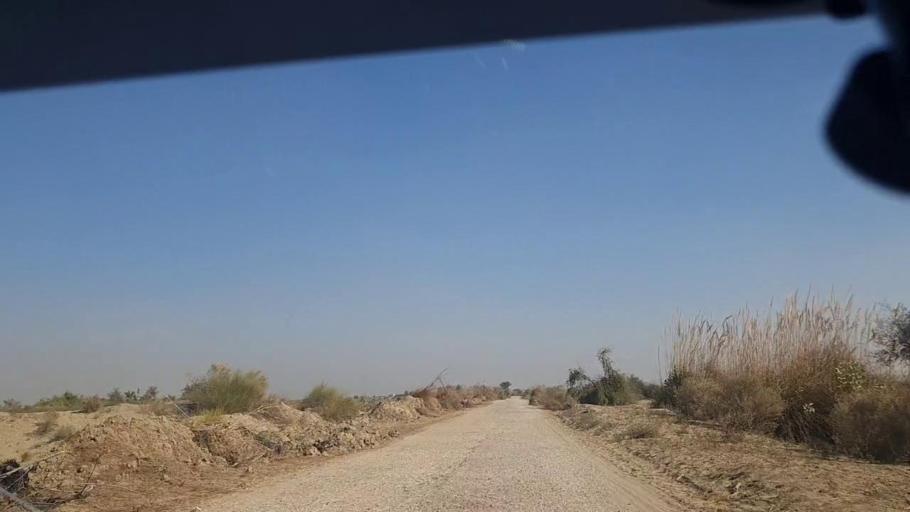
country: PK
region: Sindh
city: Khanpur
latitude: 27.5643
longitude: 69.3095
